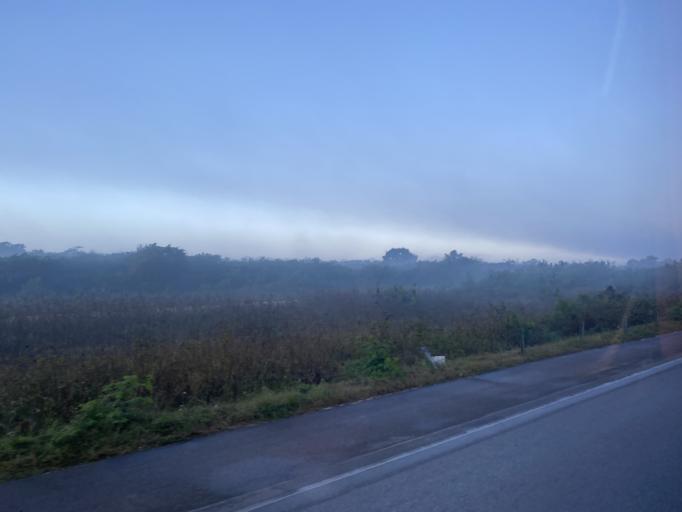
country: DO
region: La Altagracia
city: Otra Banda
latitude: 18.7325
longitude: -68.5054
